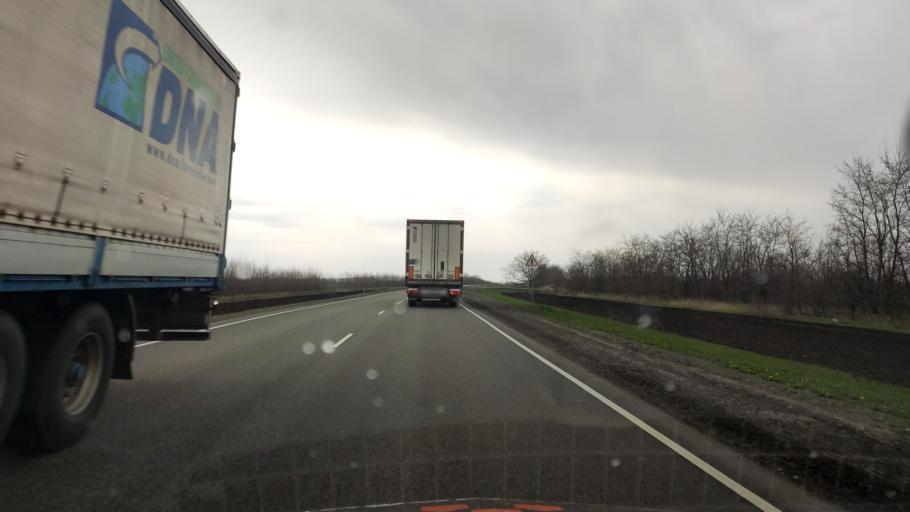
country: RU
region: Voronezj
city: Nizhnedevitsk
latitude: 51.5673
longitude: 38.3419
